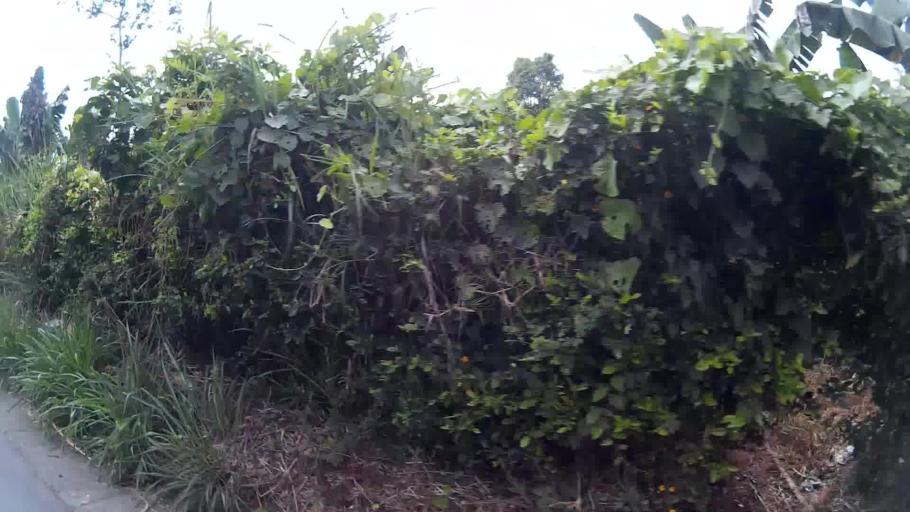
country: CO
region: Risaralda
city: Pereira
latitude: 4.8497
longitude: -75.7616
